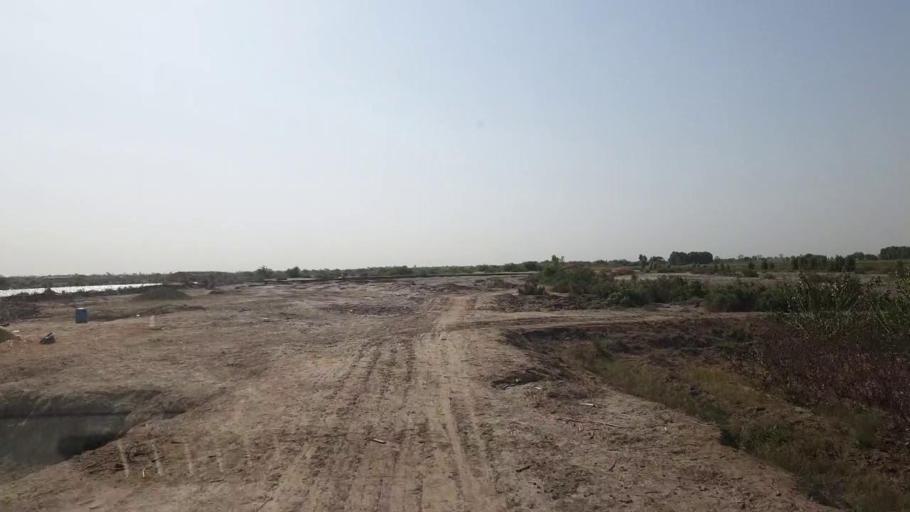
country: PK
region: Sindh
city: Kadhan
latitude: 24.6126
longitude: 69.0693
